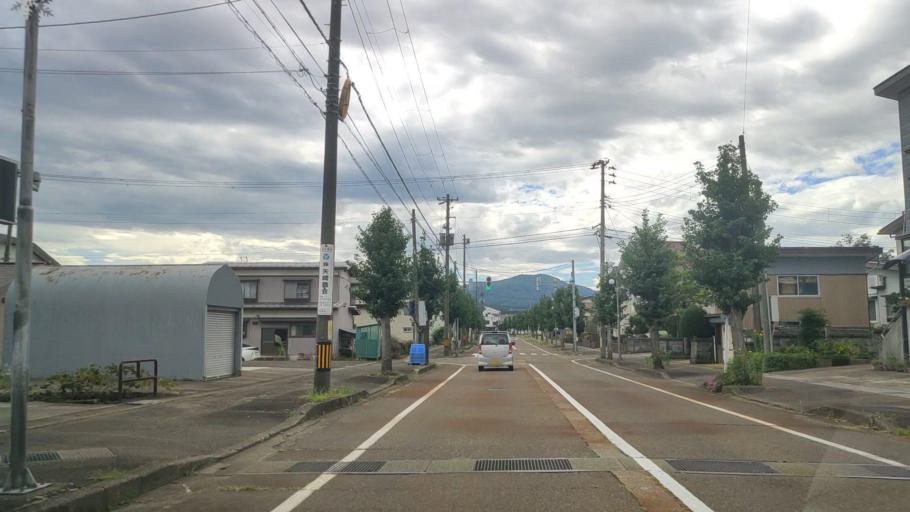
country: JP
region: Niigata
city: Arai
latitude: 37.0234
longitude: 138.2463
